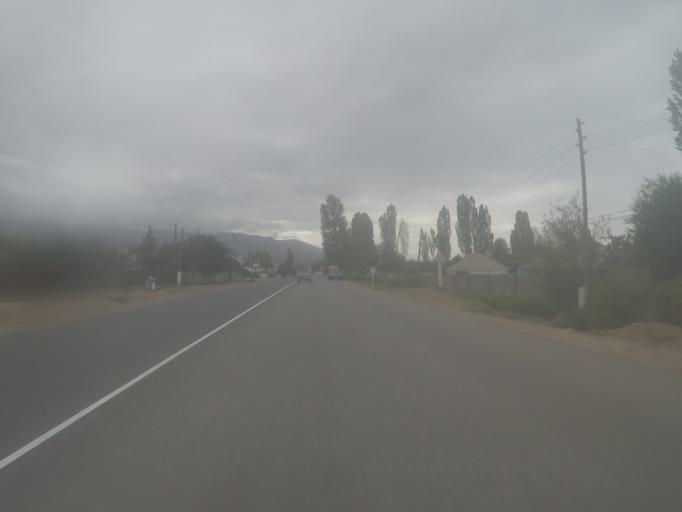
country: KG
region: Ysyk-Koel
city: Cholpon-Ata
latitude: 42.6709
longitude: 77.2931
